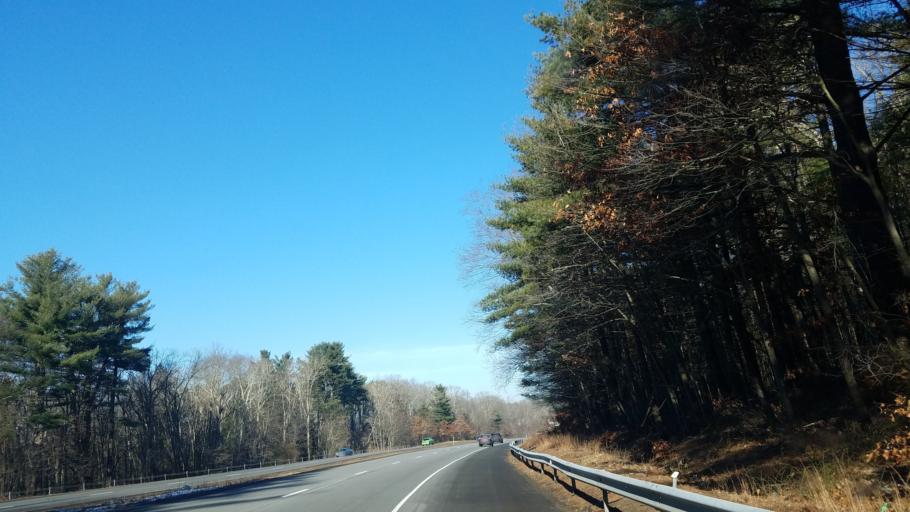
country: US
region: Connecticut
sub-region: Windham County
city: Killingly Center
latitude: 41.8276
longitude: -71.8737
